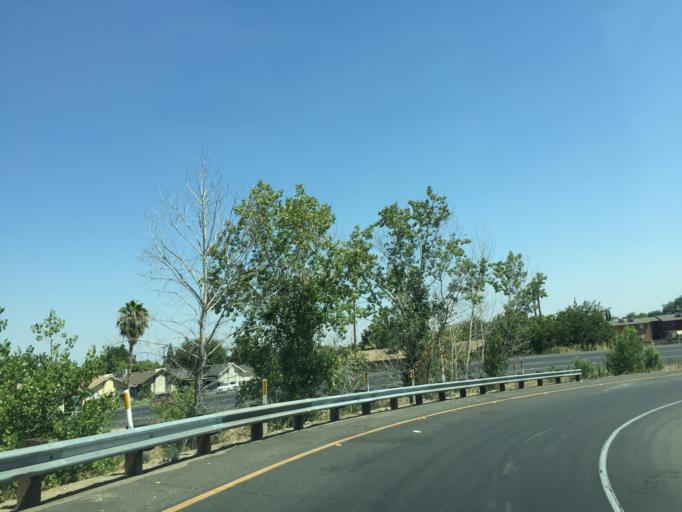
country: US
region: California
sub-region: Fresno County
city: Fresno
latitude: 36.7663
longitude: -119.7484
